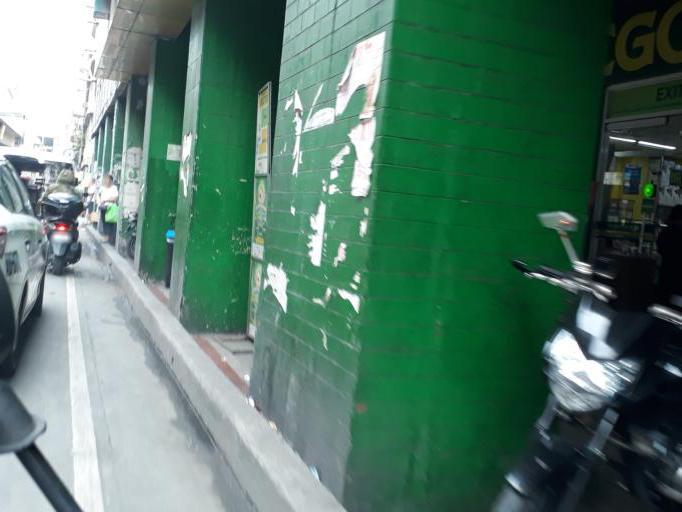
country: PH
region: Metro Manila
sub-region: City of Manila
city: Quiapo
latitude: 14.6017
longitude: 120.9817
